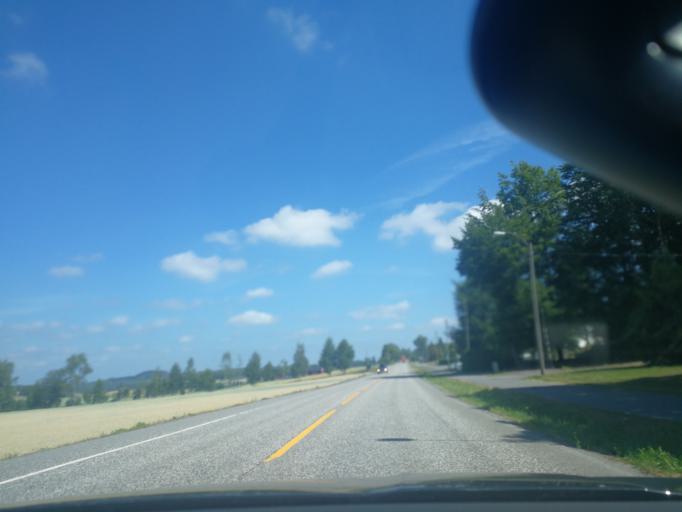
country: NO
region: Vestfold
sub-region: Sandefjord
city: Sandefjord
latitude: 59.1853
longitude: 10.2180
